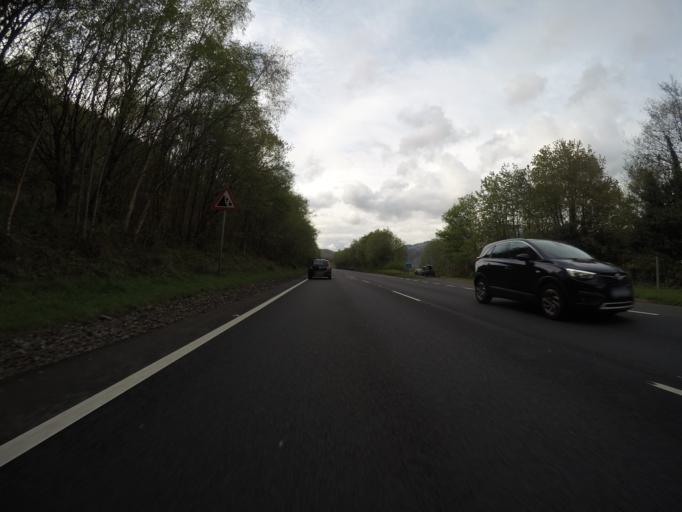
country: GB
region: Scotland
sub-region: Argyll and Bute
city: Helensburgh
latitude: 56.1375
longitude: -4.6597
